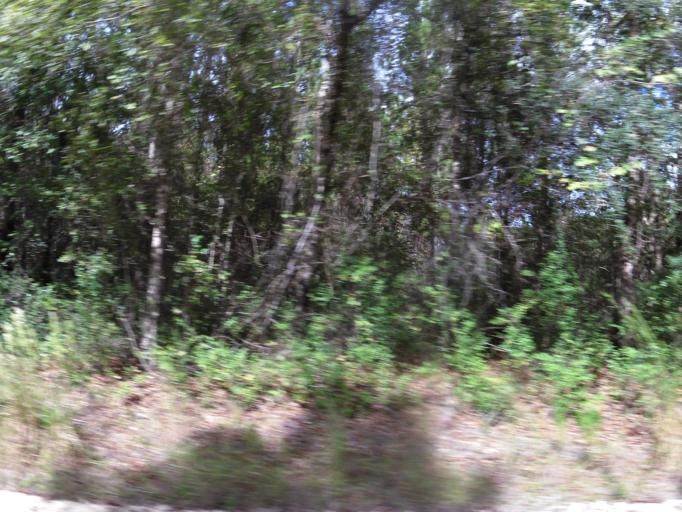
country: US
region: Florida
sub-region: Nassau County
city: Hilliard
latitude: 30.6063
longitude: -82.0726
